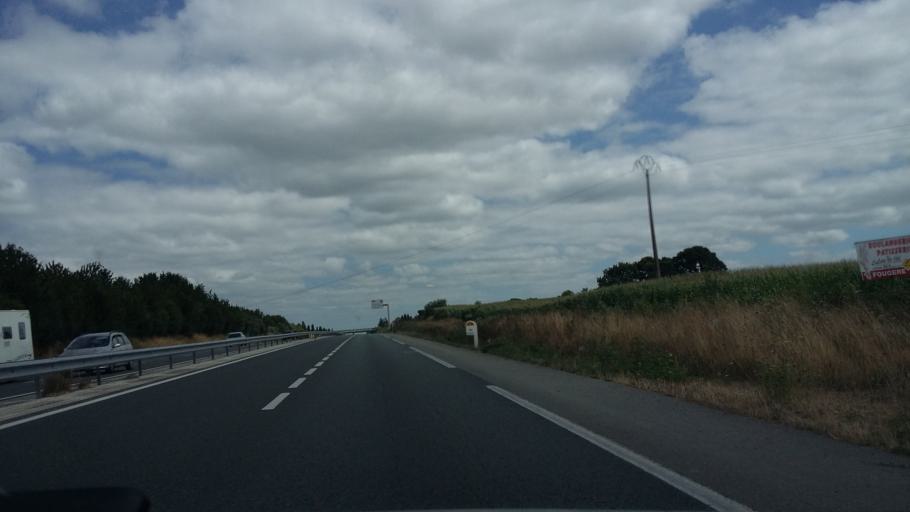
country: FR
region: Pays de la Loire
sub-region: Departement de la Vendee
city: La Chaize-le-Vicomte
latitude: 46.6551
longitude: -1.2374
